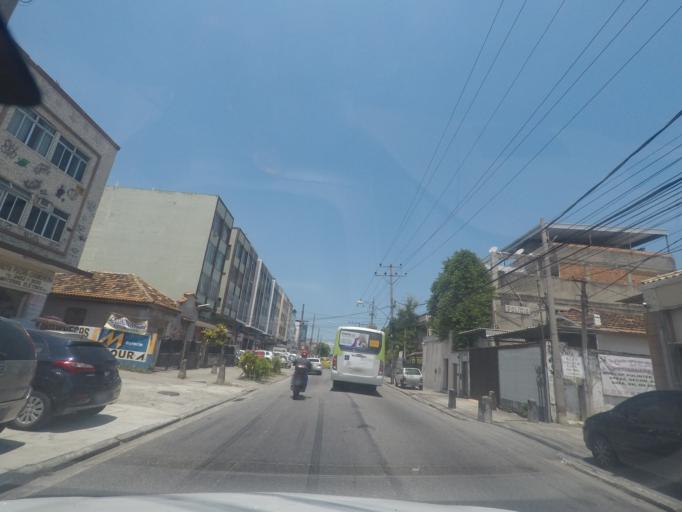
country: BR
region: Rio de Janeiro
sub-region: Duque De Caxias
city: Duque de Caxias
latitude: -22.8404
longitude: -43.3013
